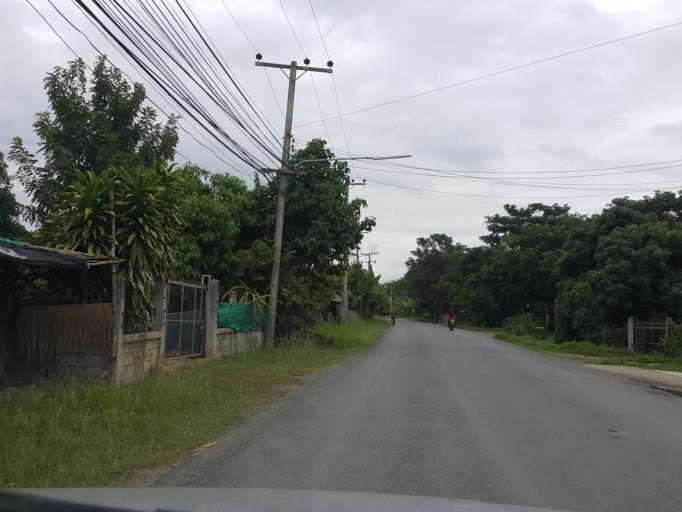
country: TH
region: Chiang Mai
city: San Kamphaeng
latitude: 18.8109
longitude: 99.1369
